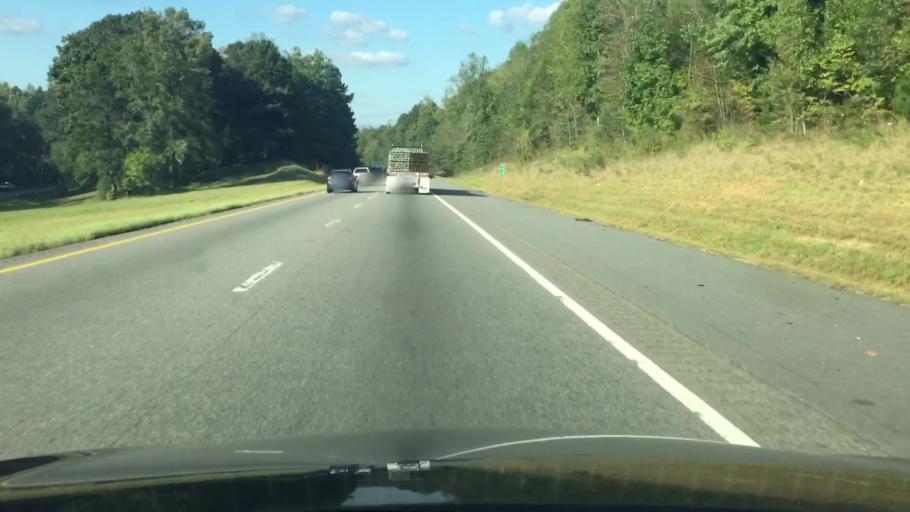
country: US
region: North Carolina
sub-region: Iredell County
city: Troutman
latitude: 35.7057
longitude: -80.8567
